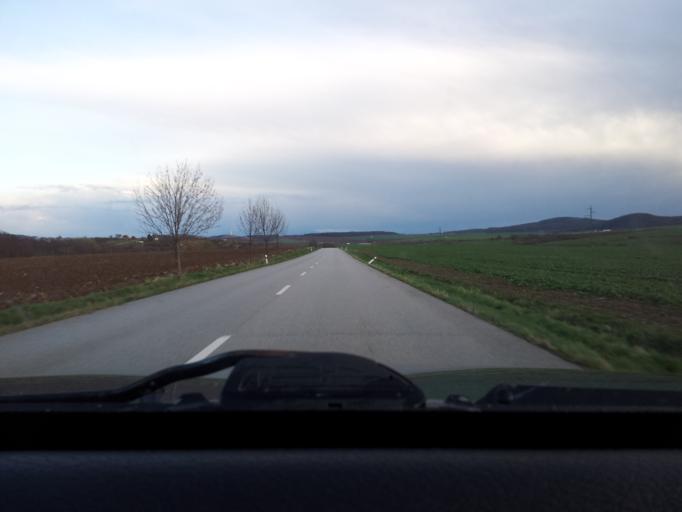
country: SK
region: Nitriansky
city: Tlmace
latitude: 48.3332
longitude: 18.4931
